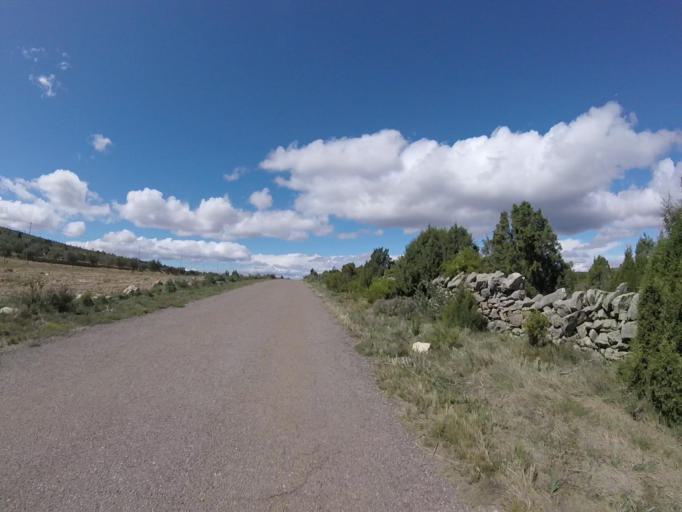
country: ES
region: Valencia
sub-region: Provincia de Castello
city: Culla
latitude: 40.3066
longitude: -0.1185
